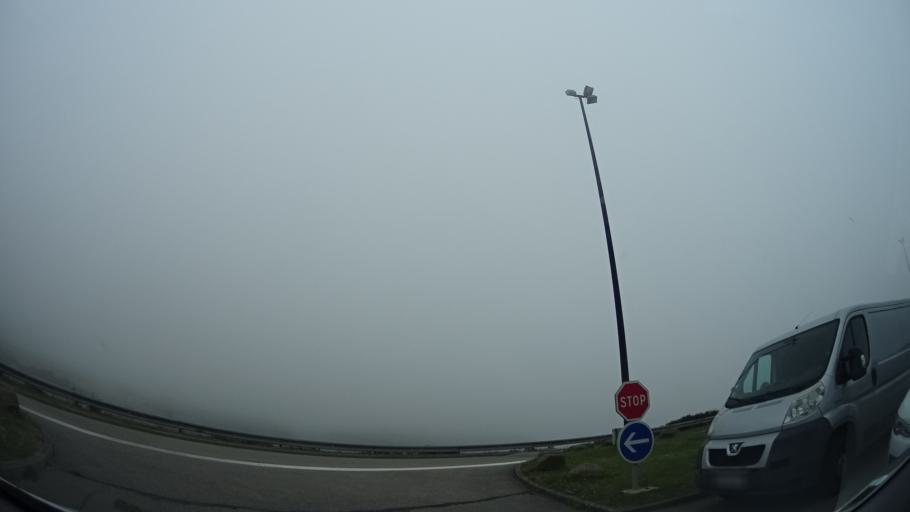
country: FR
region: Lower Normandy
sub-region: Departement de la Manche
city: Flamanville
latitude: 49.5305
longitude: -1.8821
